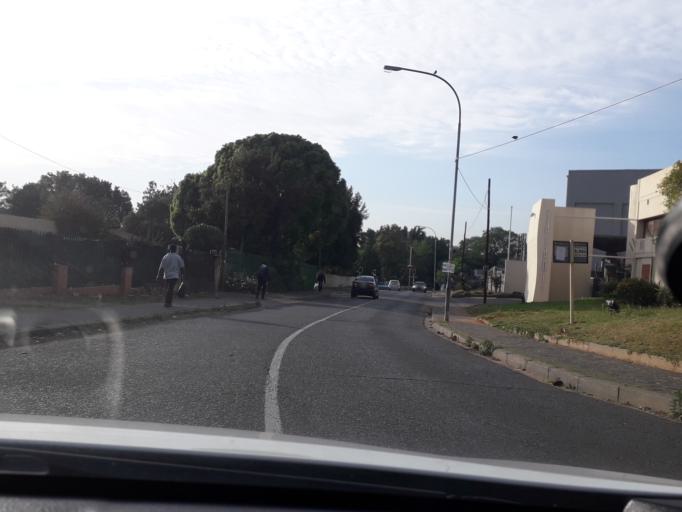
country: ZA
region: Gauteng
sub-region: City of Johannesburg Metropolitan Municipality
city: Johannesburg
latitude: -26.1341
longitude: 28.0927
